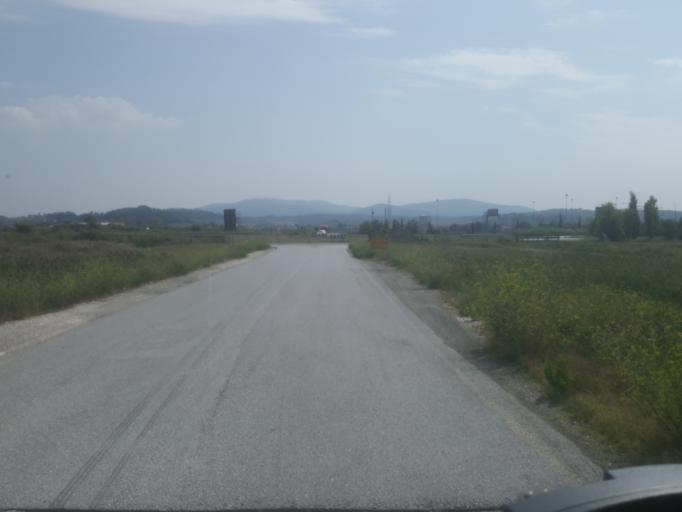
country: IT
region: Tuscany
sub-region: Provincia di Livorno
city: Guasticce
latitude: 43.6083
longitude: 10.4076
